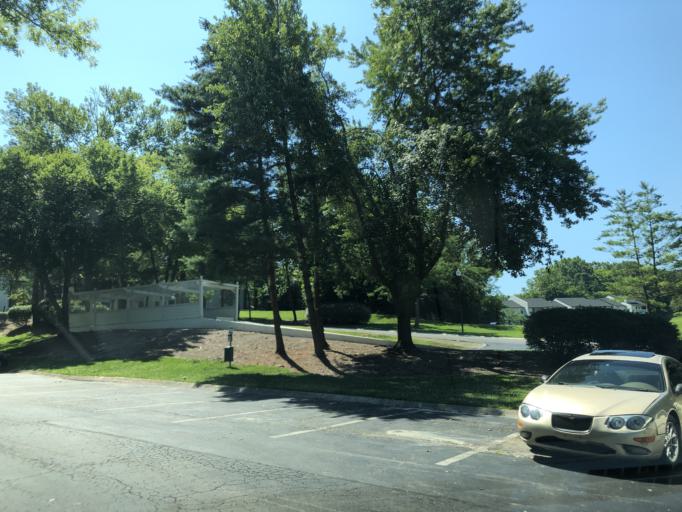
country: US
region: Tennessee
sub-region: Rutherford County
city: La Vergne
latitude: 36.0433
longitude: -86.6673
